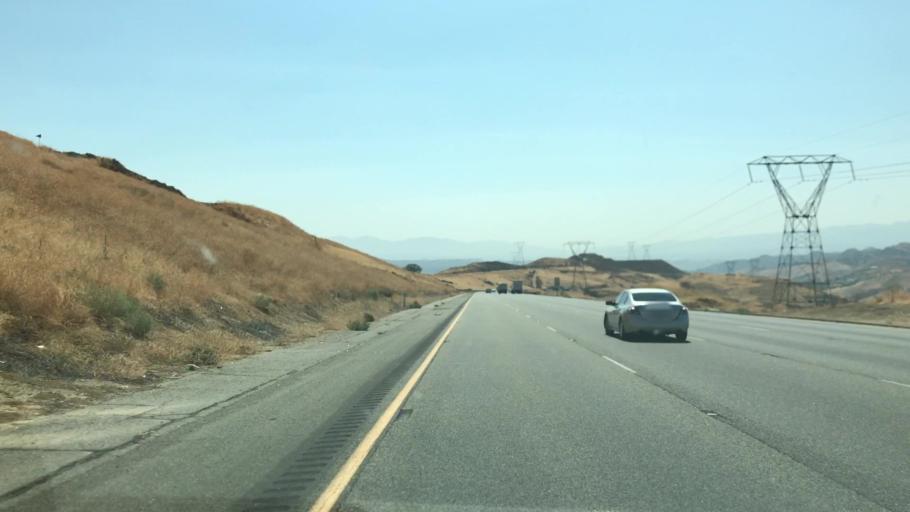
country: US
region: California
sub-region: Los Angeles County
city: Castaic
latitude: 34.5399
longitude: -118.6495
